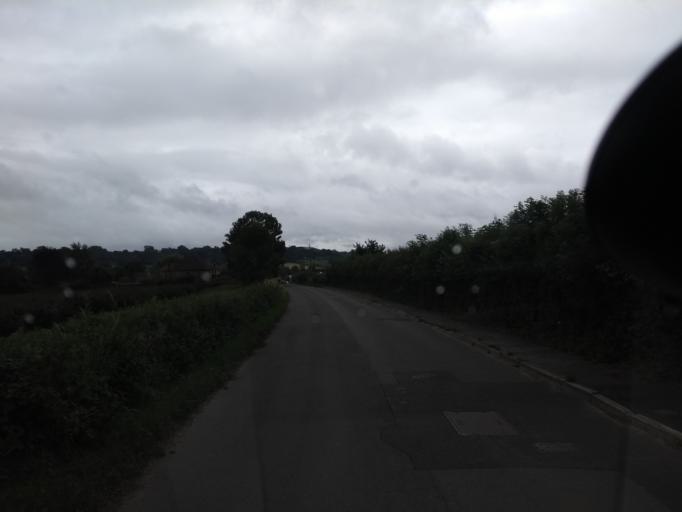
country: GB
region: England
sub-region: Somerset
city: Stoke-sub-Hamdon
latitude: 50.9473
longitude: -2.7562
